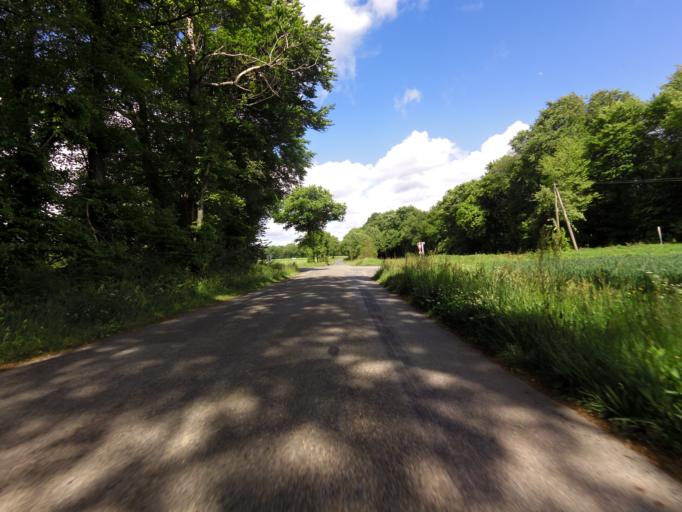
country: FR
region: Brittany
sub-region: Departement du Morbihan
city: Pluherlin
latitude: 47.7261
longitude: -2.3669
